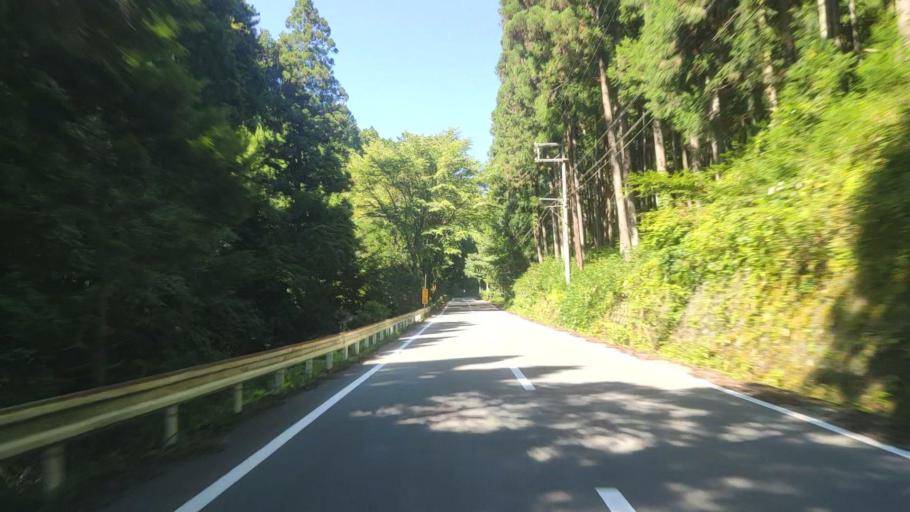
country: JP
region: Nara
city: Yoshino-cho
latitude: 34.4162
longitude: 135.9351
